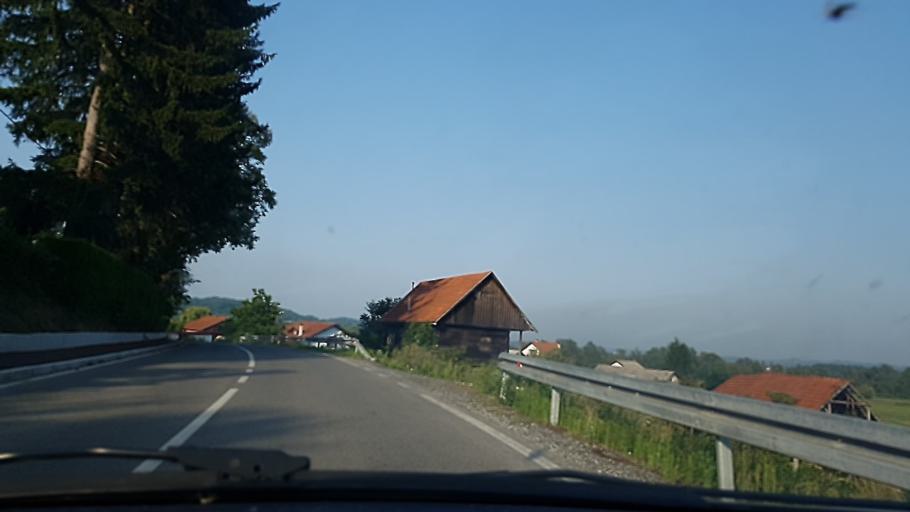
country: HR
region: Zagrebacka
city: Jakovlje
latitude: 46.0053
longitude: 15.8503
